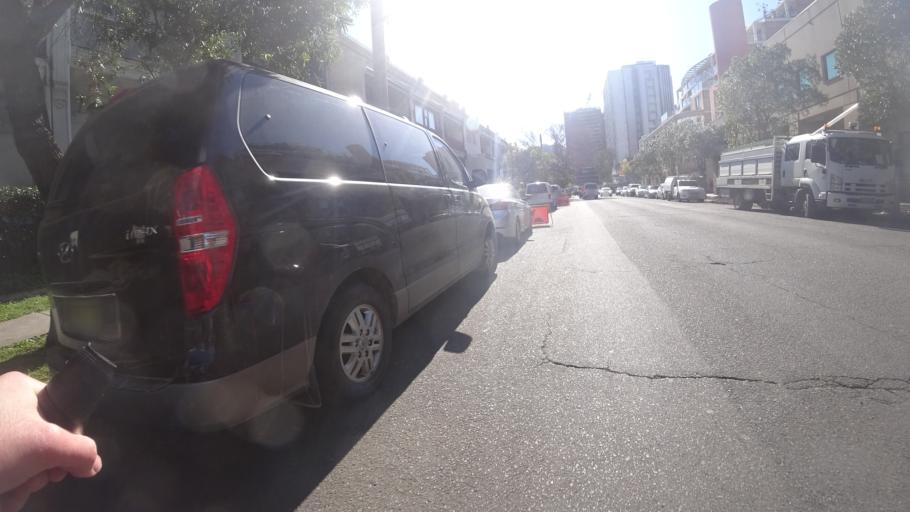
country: AU
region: New South Wales
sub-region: Waverley
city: Bondi Junction
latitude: -33.8928
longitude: 151.2448
